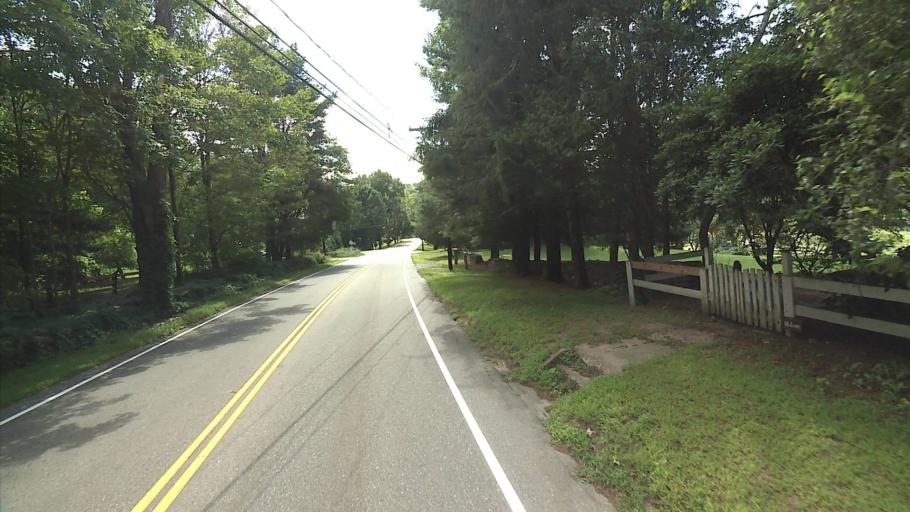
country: US
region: Connecticut
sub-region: Windham County
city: South Woodstock
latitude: 41.9431
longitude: -72.0745
